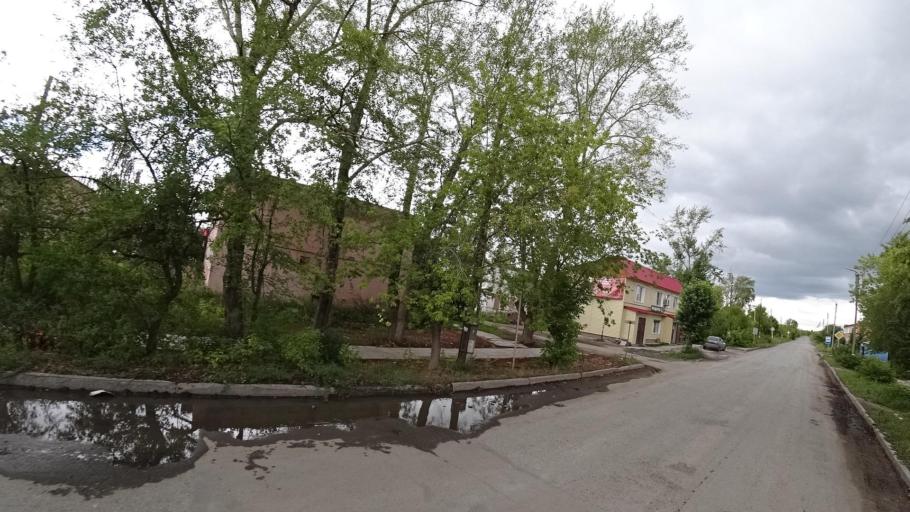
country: RU
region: Sverdlovsk
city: Kamyshlov
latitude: 56.8533
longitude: 62.7288
